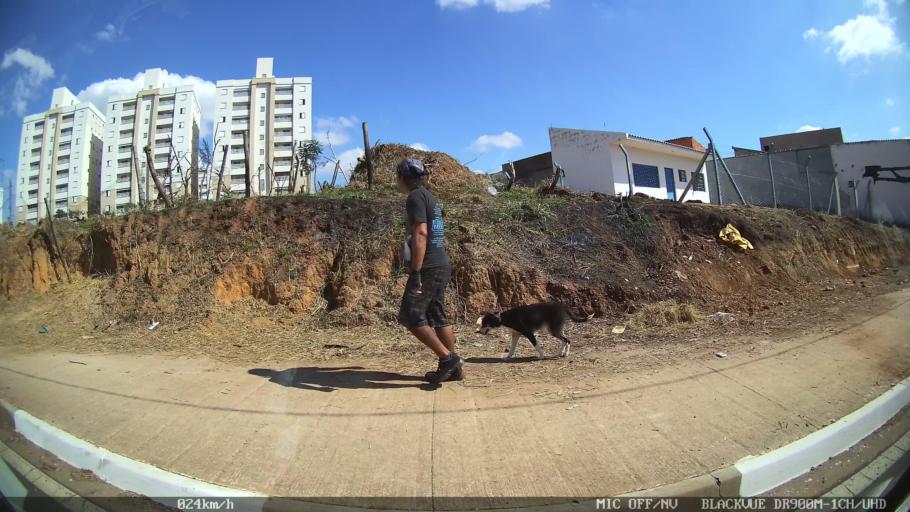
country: BR
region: Sao Paulo
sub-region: Hortolandia
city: Hortolandia
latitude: -22.8942
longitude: -47.1960
